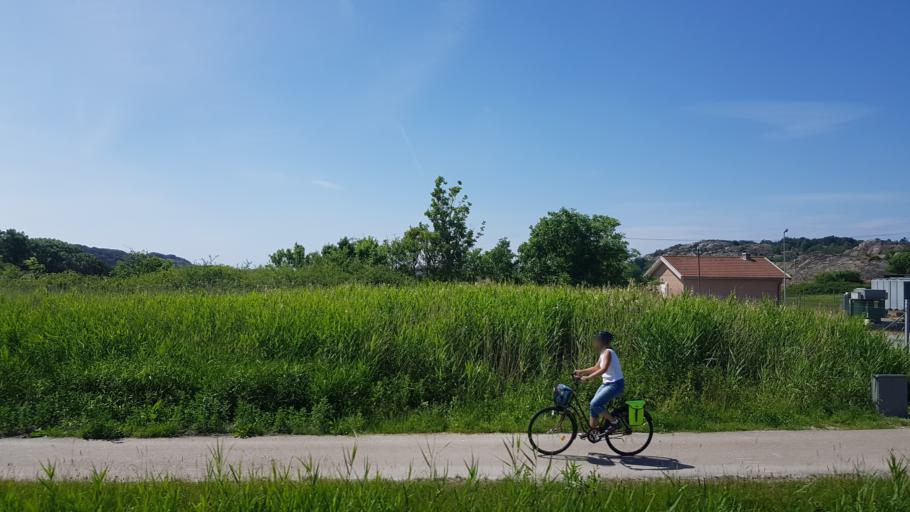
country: SE
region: Vaestra Goetaland
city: Ronnang
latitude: 57.9627
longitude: 11.5765
